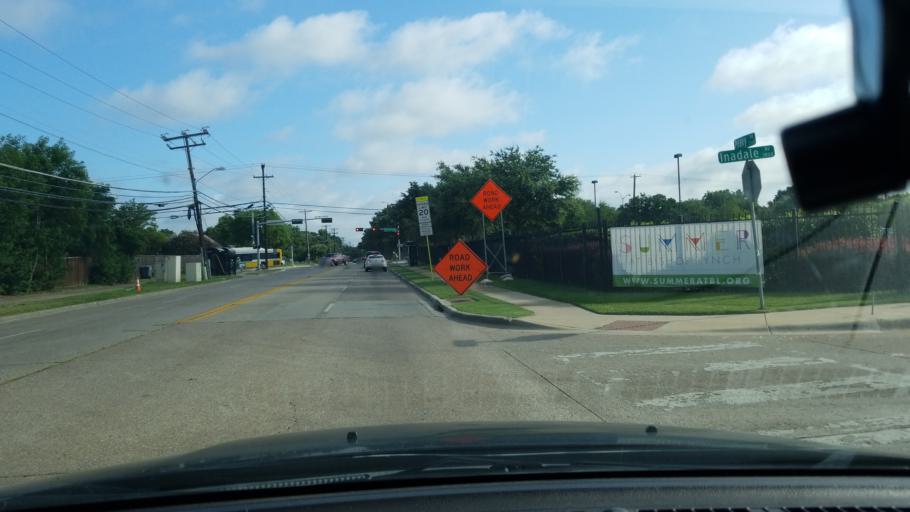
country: US
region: Texas
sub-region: Dallas County
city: Mesquite
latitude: 32.8178
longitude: -96.6844
